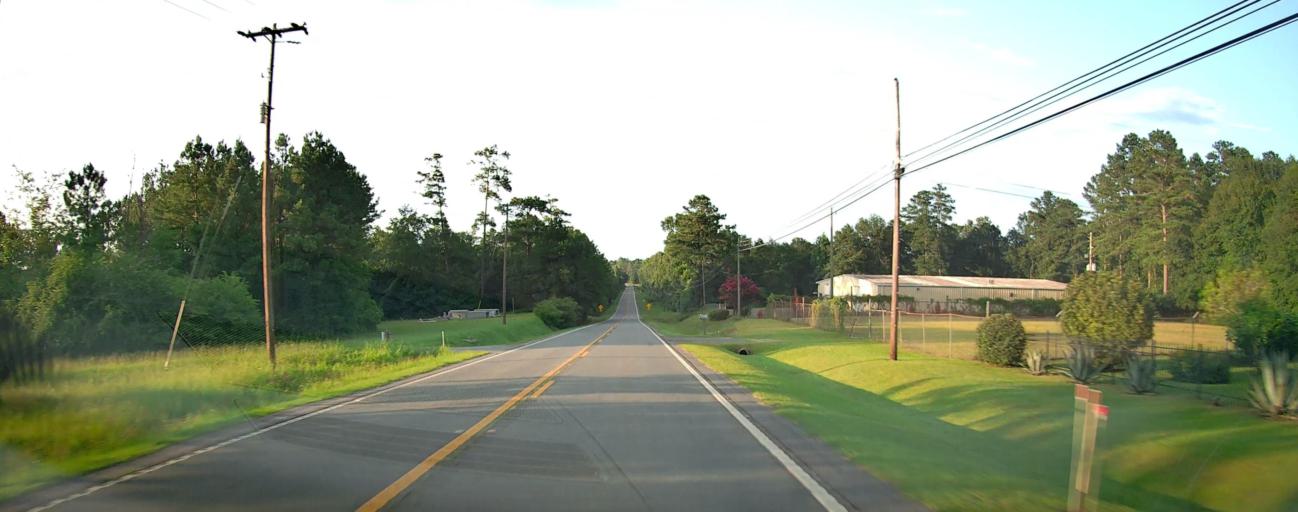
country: US
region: Georgia
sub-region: Taylor County
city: Reynolds
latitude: 32.5680
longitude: -84.0936
